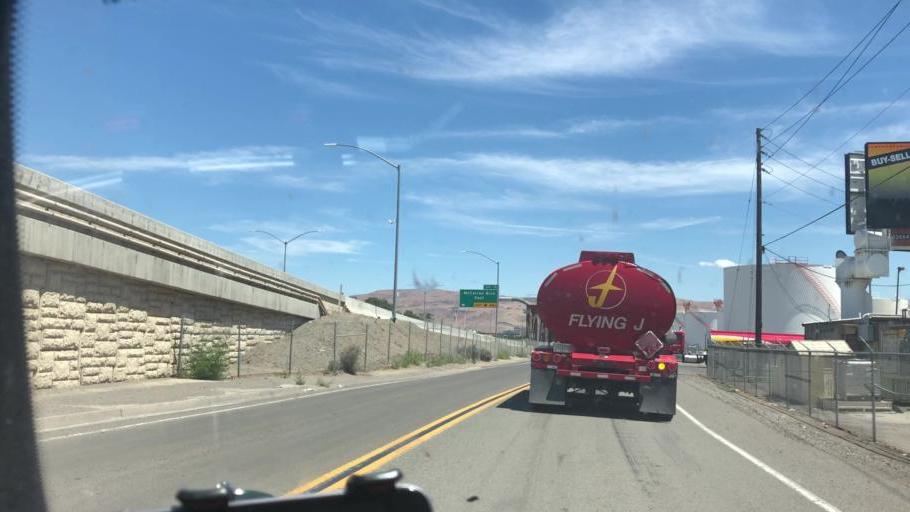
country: US
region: Nevada
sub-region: Washoe County
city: Sparks
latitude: 39.5340
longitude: -119.7496
